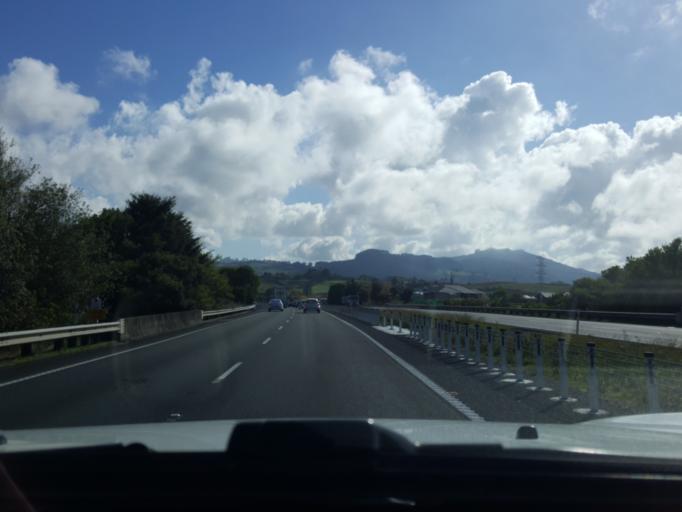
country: NZ
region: Auckland
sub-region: Auckland
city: Pukekohe East
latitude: -37.2487
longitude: 175.0282
